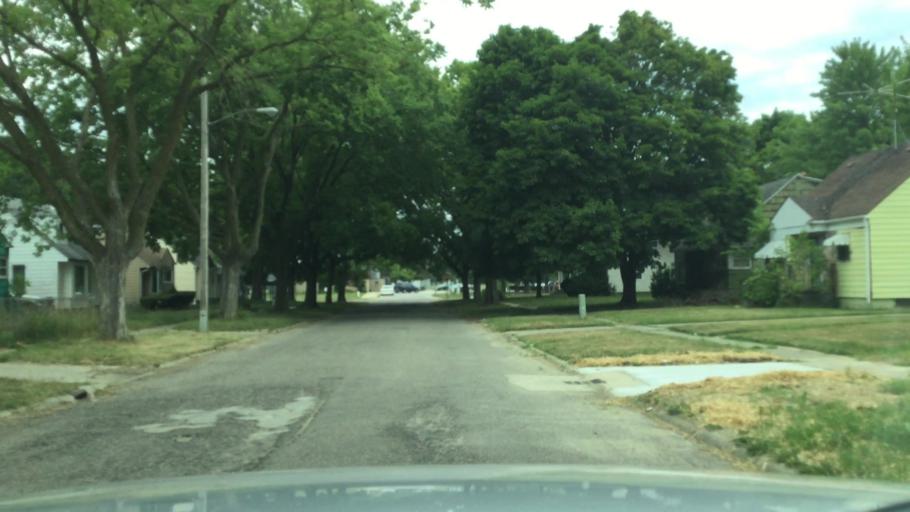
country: US
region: Michigan
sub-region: Genesee County
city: Beecher
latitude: 43.0660
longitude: -83.7173
